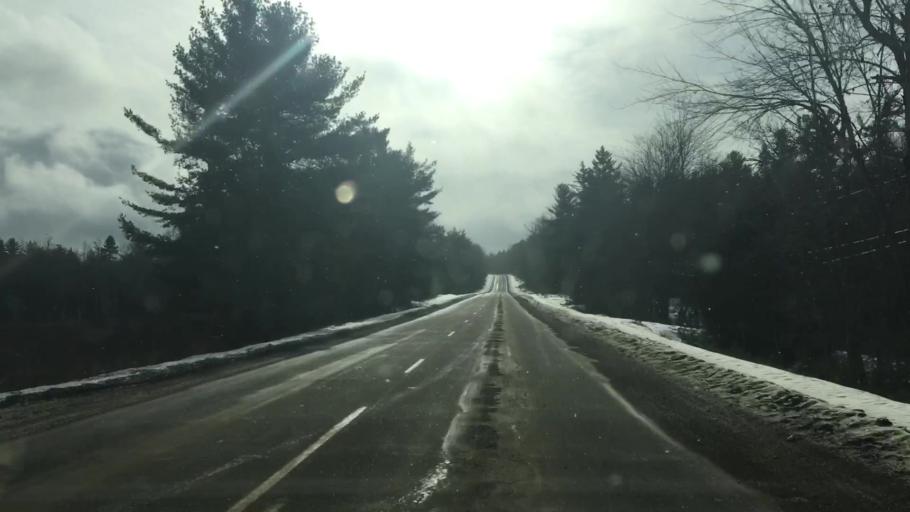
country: US
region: Maine
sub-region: Washington County
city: Calais
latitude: 45.0731
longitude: -67.3319
